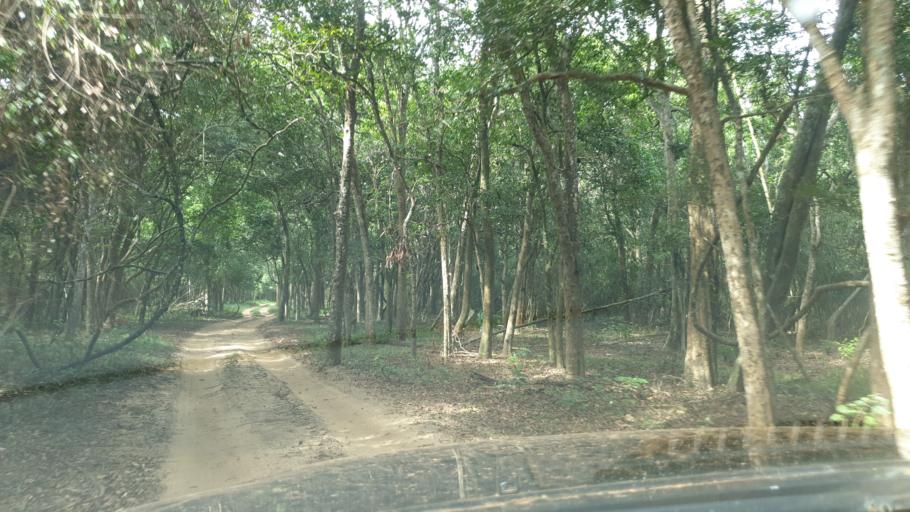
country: LK
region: North Western
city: Puttalam
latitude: 8.4119
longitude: 79.9846
